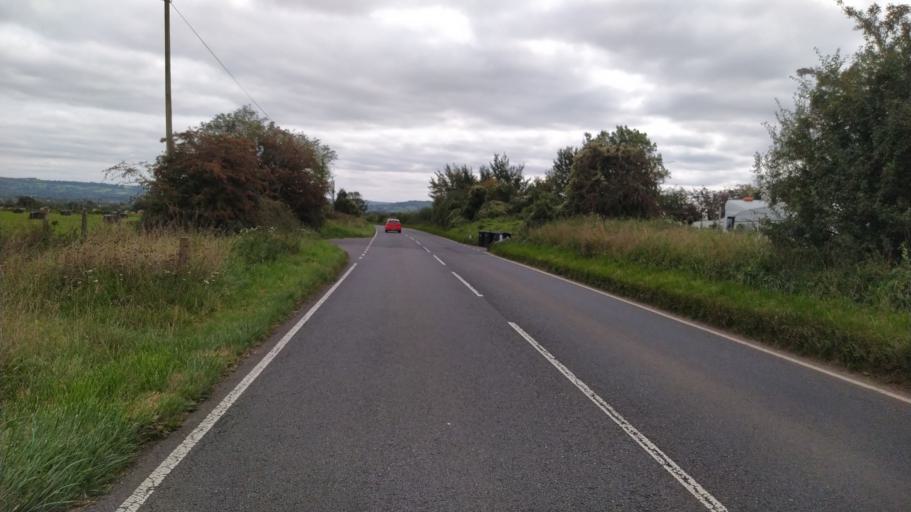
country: GB
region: England
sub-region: Dorset
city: Gillingham
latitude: 51.0486
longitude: -2.3238
